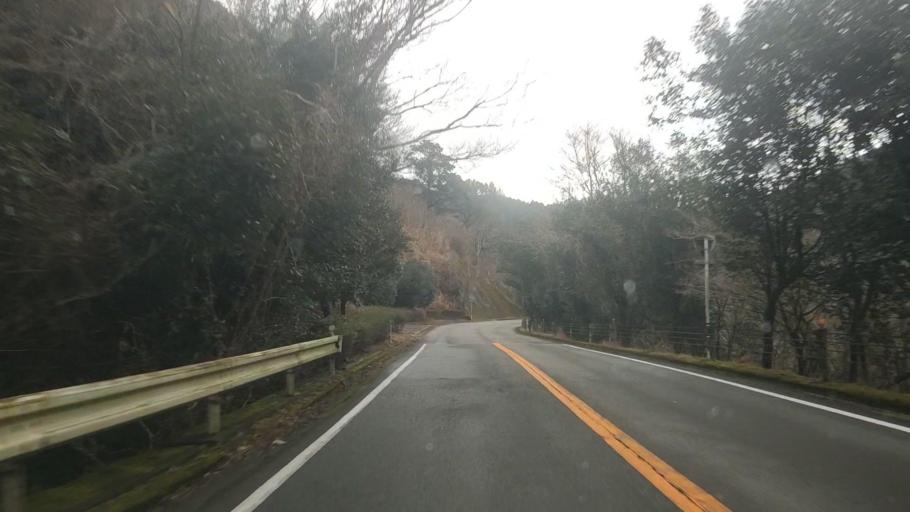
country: JP
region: Kumamoto
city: Hitoyoshi
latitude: 32.1253
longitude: 130.8128
